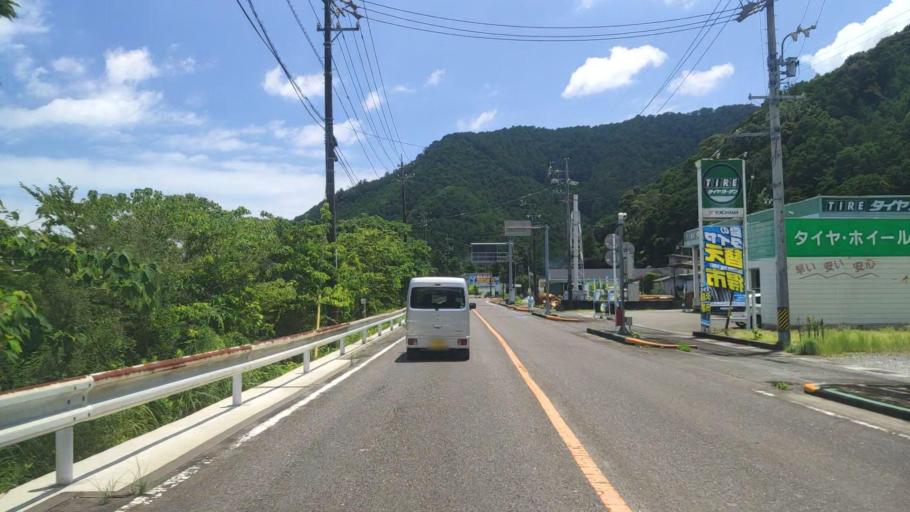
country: JP
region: Mie
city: Owase
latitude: 34.1188
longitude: 136.2194
